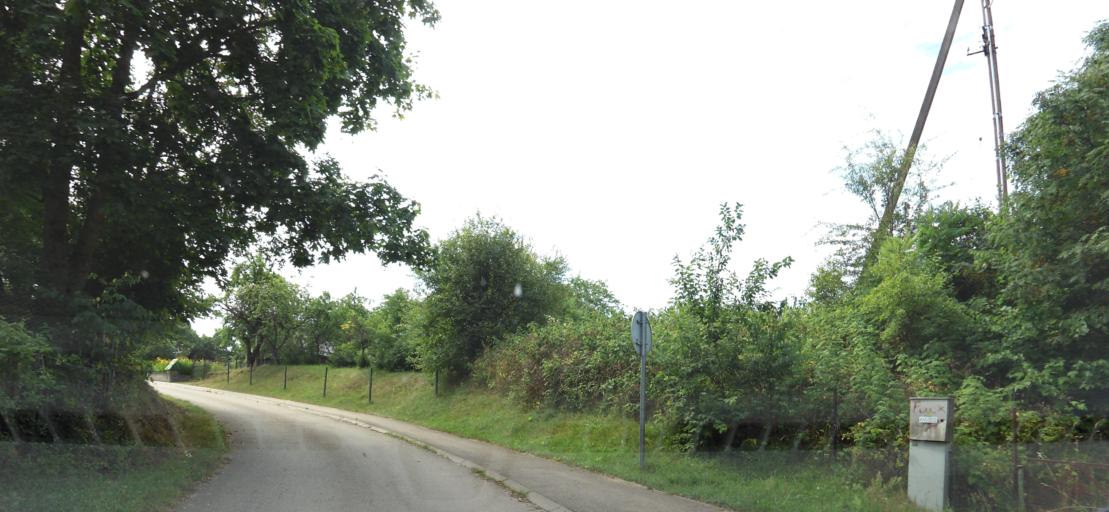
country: LT
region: Vilnius County
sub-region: Trakai
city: Rudiskes
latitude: 54.3560
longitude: 24.8417
